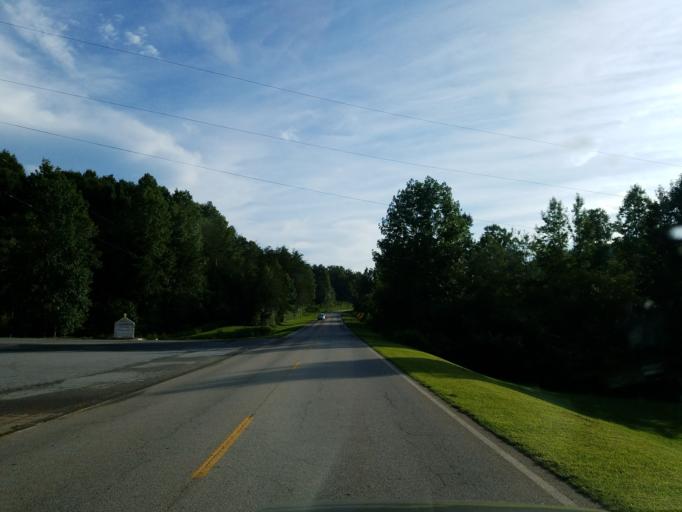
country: US
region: Georgia
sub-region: Lumpkin County
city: Dahlonega
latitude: 34.5267
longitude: -83.9067
